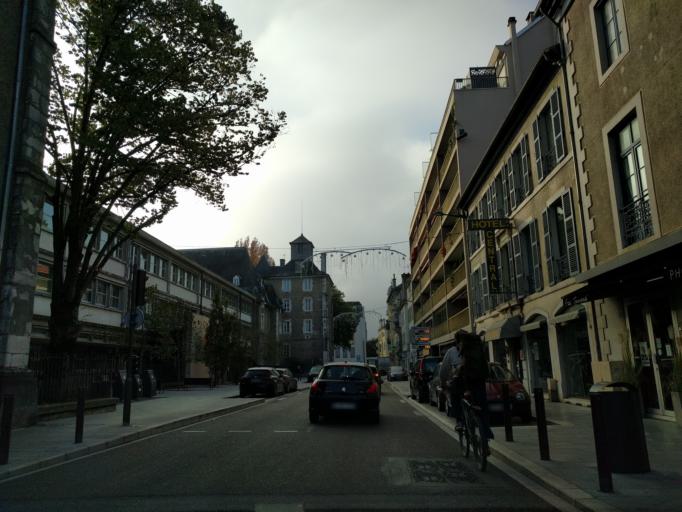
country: FR
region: Aquitaine
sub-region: Departement des Pyrenees-Atlantiques
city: Pau
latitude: 43.2958
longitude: -0.3661
